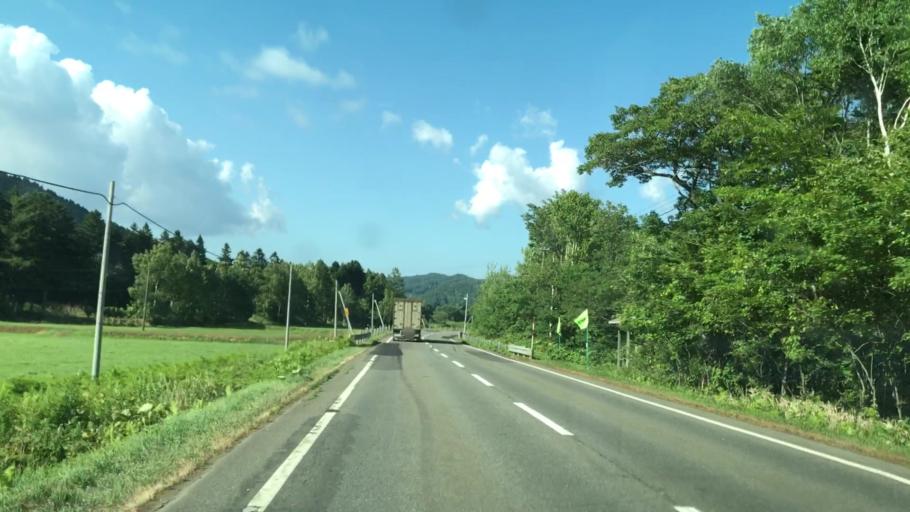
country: JP
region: Hokkaido
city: Shimo-furano
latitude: 42.8645
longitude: 142.4234
